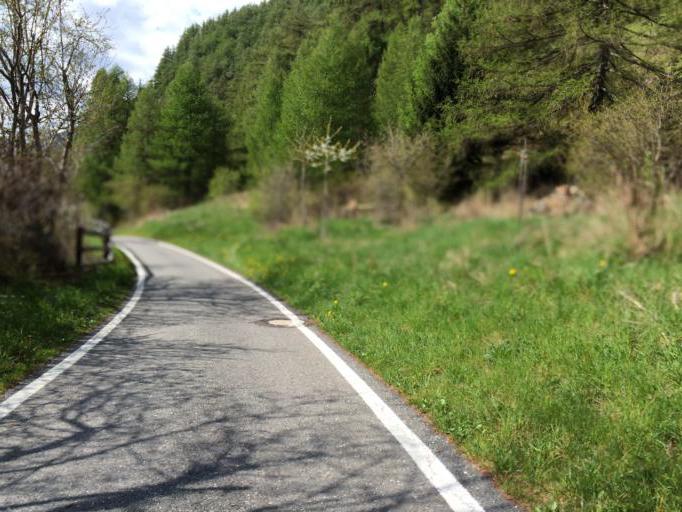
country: IT
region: Trentino-Alto Adige
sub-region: Bolzano
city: Malles Venosta
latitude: 46.7282
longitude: 10.5297
